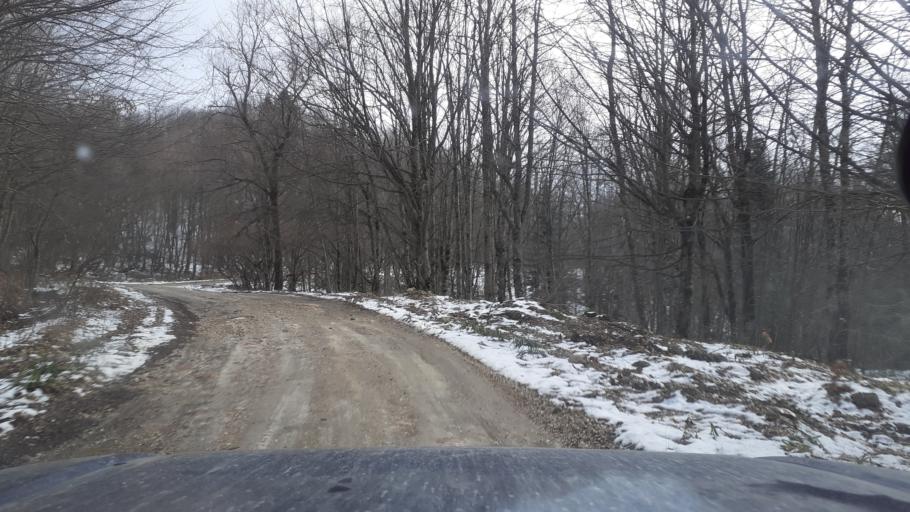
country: RU
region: Krasnodarskiy
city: Neftegorsk
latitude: 44.0738
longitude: 39.7620
